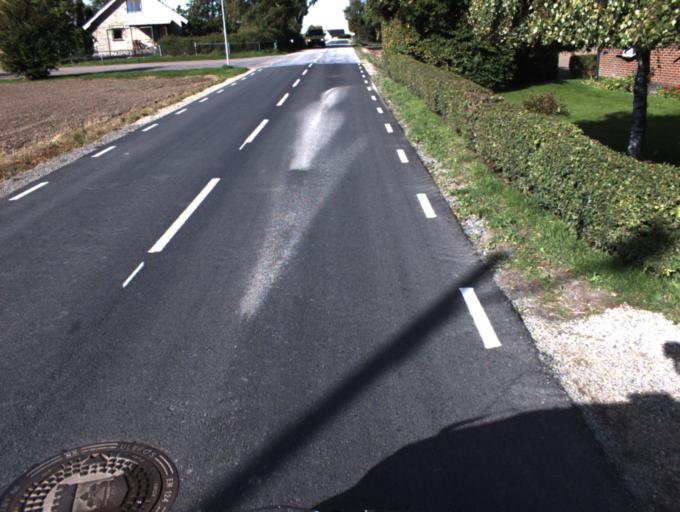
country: SE
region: Skane
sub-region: Helsingborg
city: Glumslov
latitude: 55.9623
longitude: 12.8458
